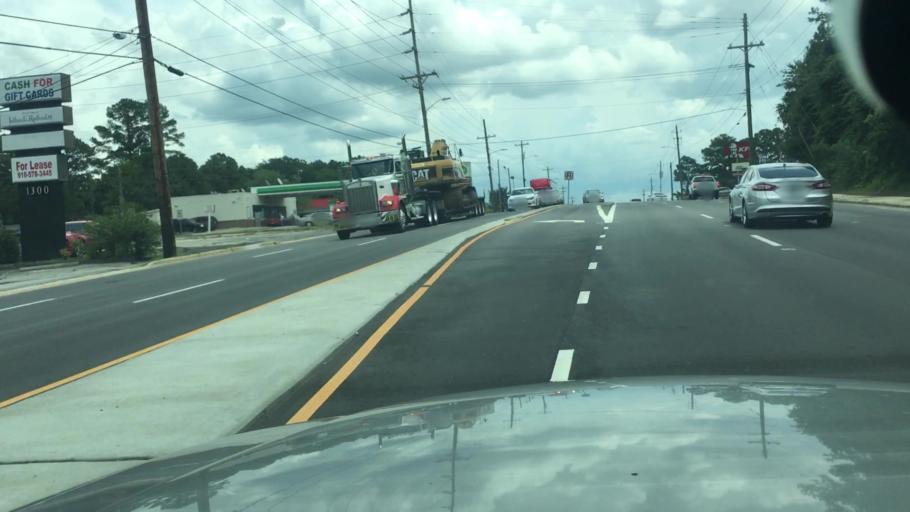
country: US
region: North Carolina
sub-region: Cumberland County
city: Fayetteville
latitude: 35.0671
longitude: -78.9016
